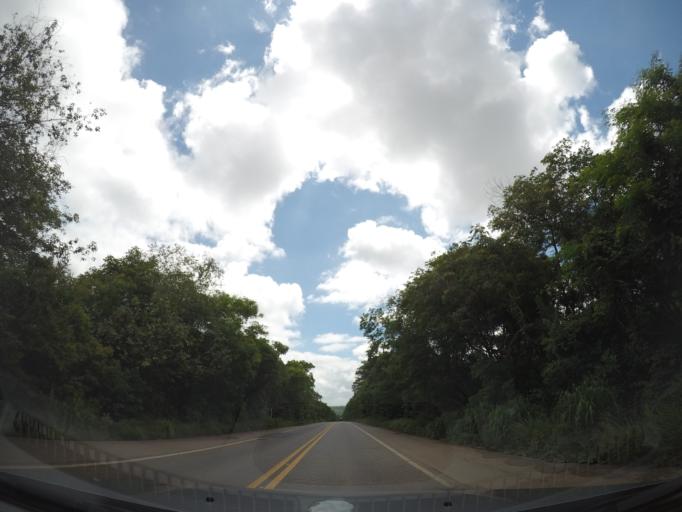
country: BR
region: Bahia
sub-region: Andarai
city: Vera Cruz
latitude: -12.4823
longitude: -41.3522
